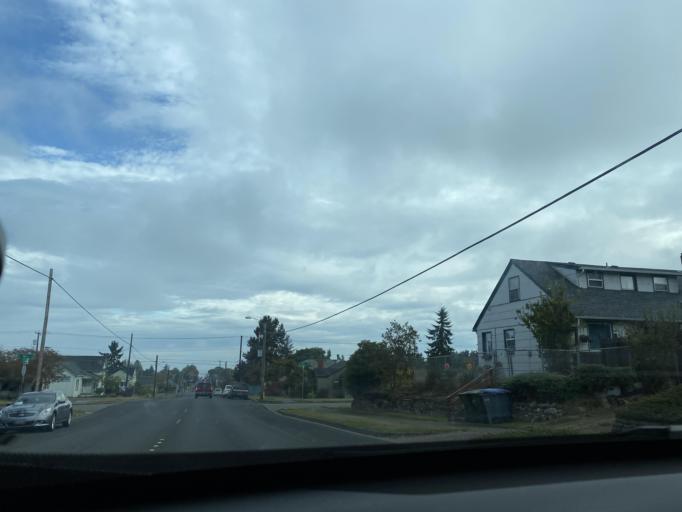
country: US
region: Washington
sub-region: Clallam County
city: Port Angeles
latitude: 48.1086
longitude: -123.4355
